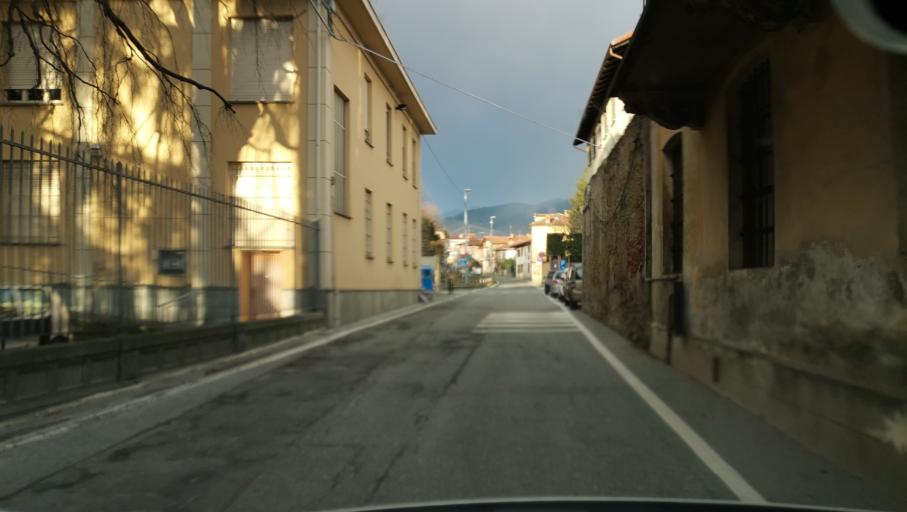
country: IT
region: Piedmont
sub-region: Provincia di Torino
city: Giaveno
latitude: 45.0448
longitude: 7.3529
